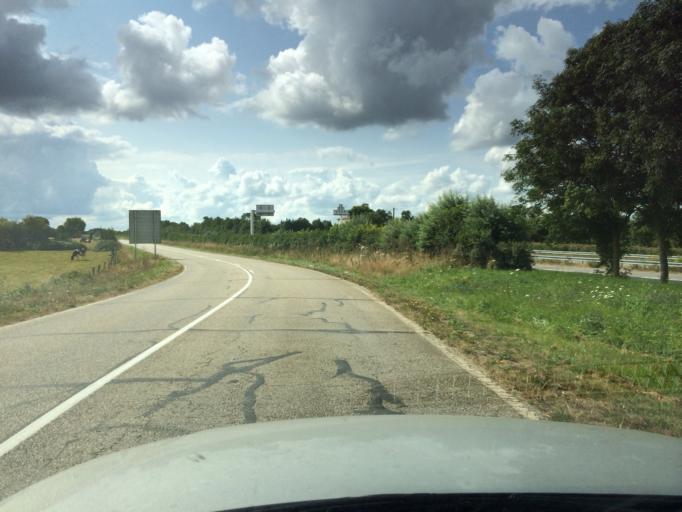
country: FR
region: Lower Normandy
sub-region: Departement de la Manche
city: Sainte-Mere-Eglise
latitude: 49.4244
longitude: -1.3291
